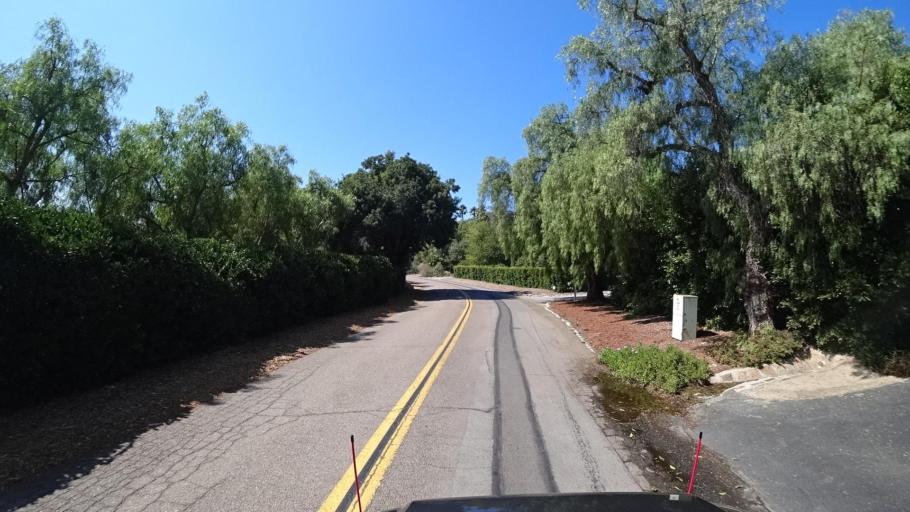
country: US
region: California
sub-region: San Diego County
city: Rancho Santa Fe
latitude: 33.0108
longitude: -117.2094
